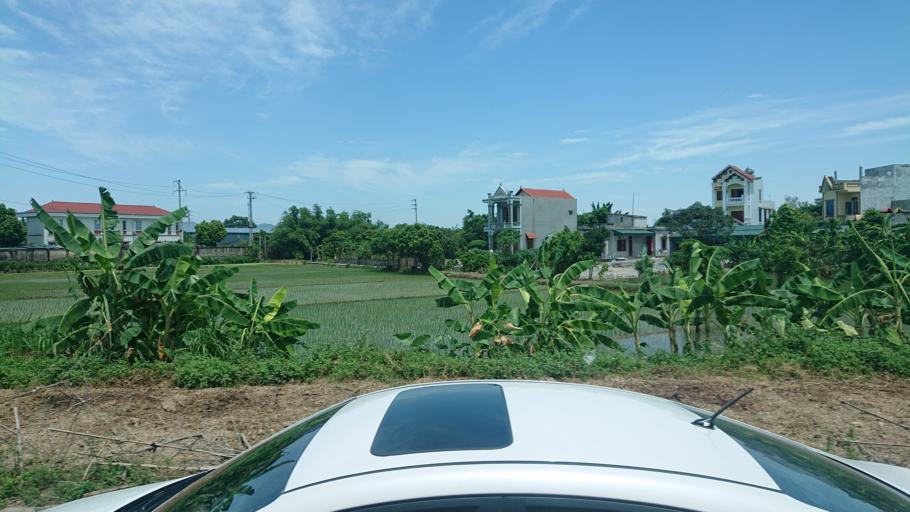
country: VN
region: Ha Nam
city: Thanh Pho Phu Ly
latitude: 20.5212
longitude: 105.9448
